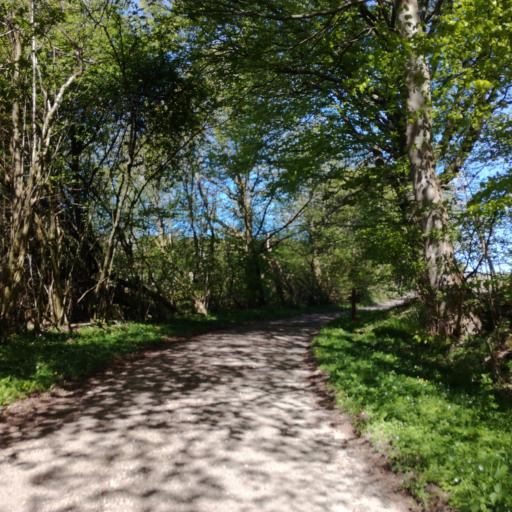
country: DK
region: South Denmark
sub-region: Vejle Kommune
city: Borkop
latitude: 55.6114
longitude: 9.6864
